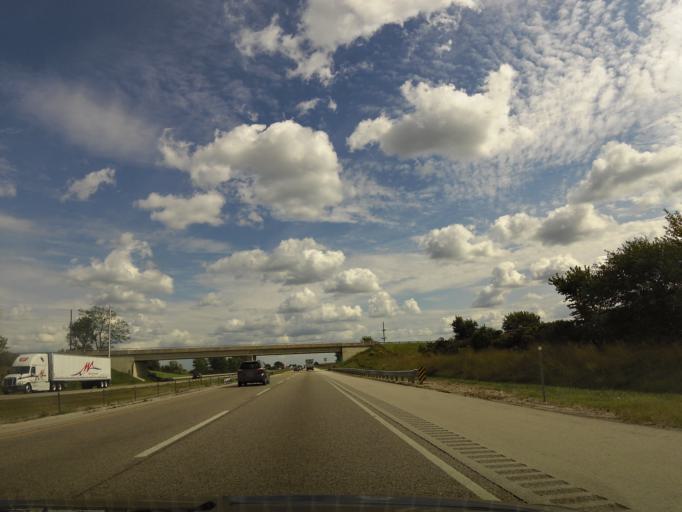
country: US
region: Illinois
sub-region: Kane County
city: Maple Park
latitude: 41.8955
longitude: -88.6408
